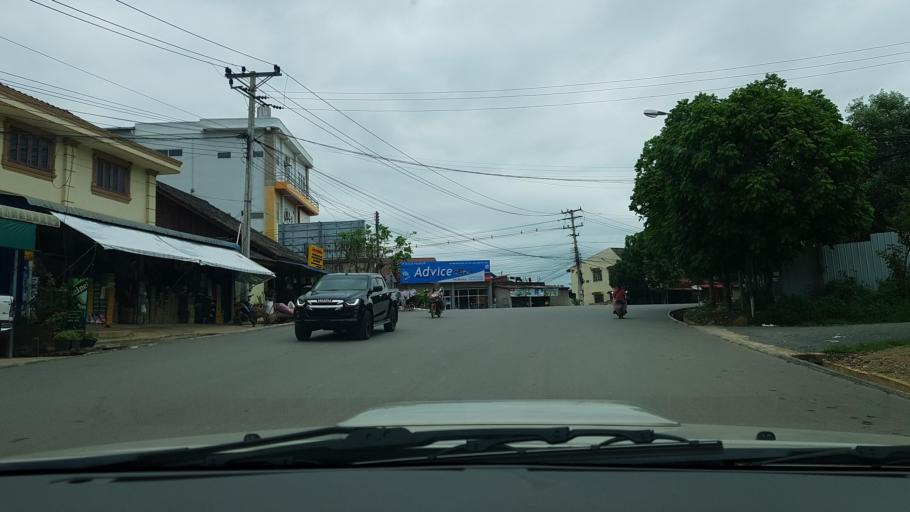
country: LA
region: Oudomxai
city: Muang Xay
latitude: 20.6949
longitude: 101.9884
